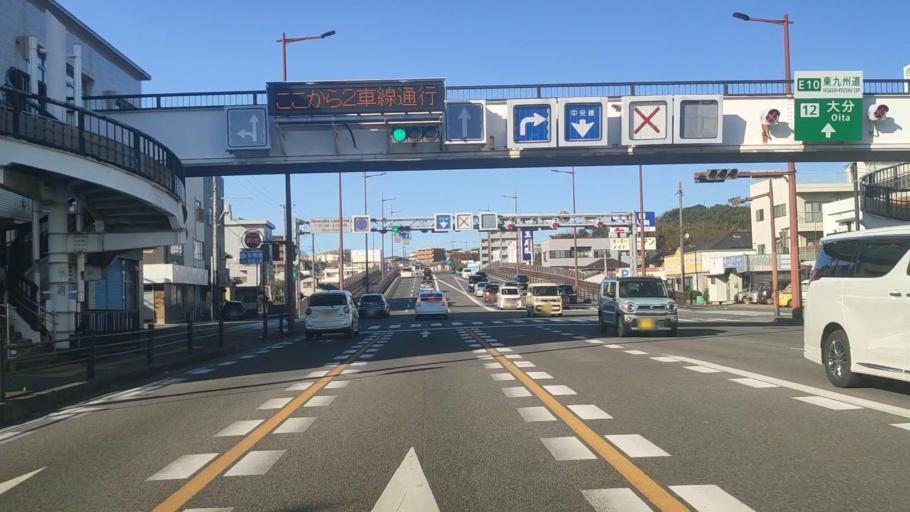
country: JP
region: Oita
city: Oita
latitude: 33.2154
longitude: 131.5958
